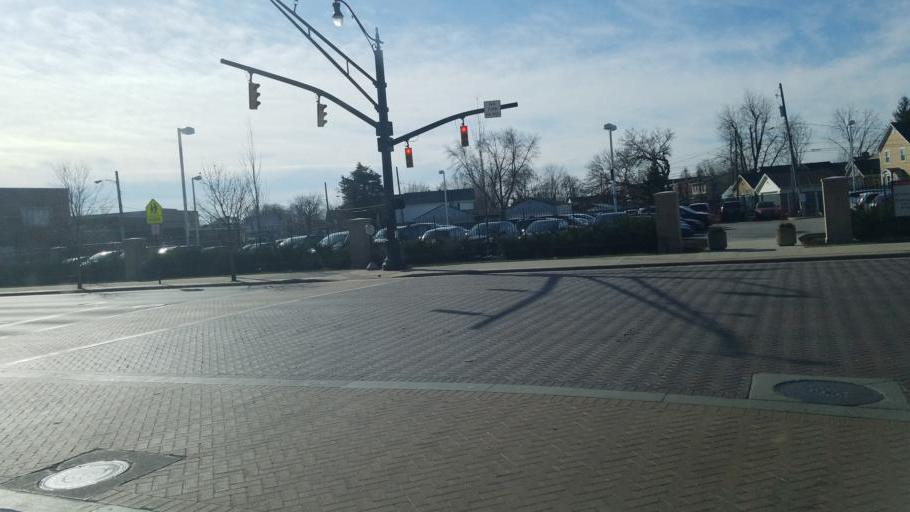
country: US
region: Ohio
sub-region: Franklin County
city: Columbus
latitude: 39.9505
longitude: -82.9766
